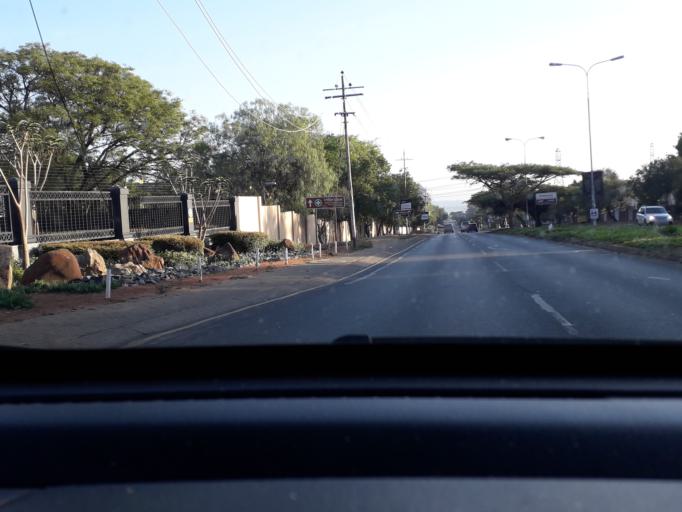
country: ZA
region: Gauteng
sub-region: City of Johannesburg Metropolitan Municipality
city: Modderfontein
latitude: -26.0891
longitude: 28.0576
